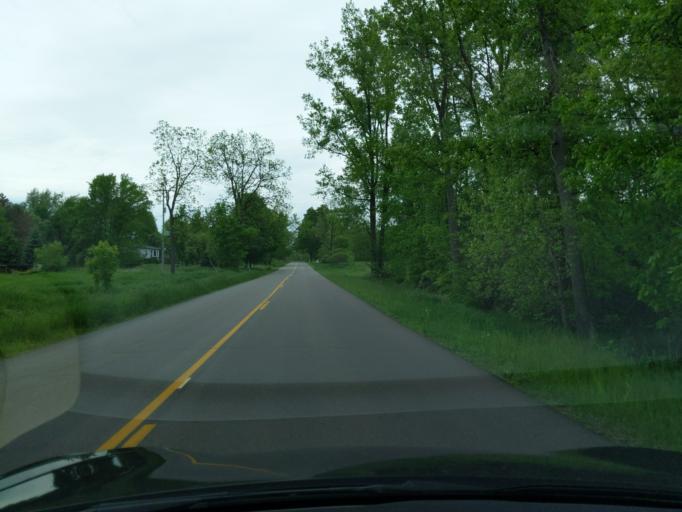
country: US
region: Michigan
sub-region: Ingham County
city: Leslie
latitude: 42.4125
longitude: -84.3530
